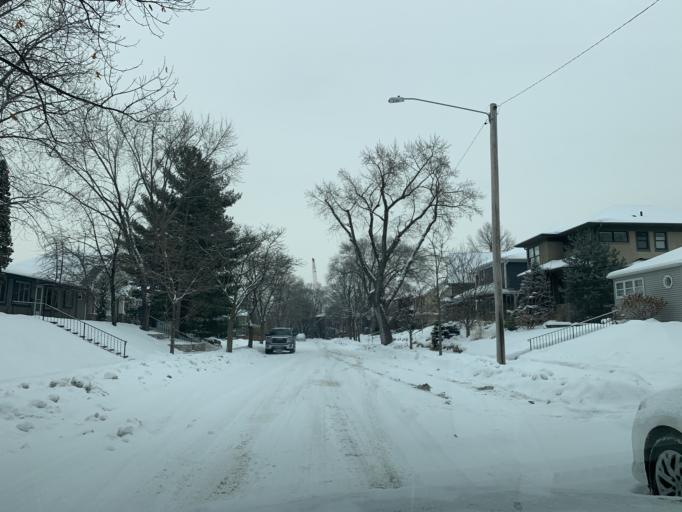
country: US
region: Minnesota
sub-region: Hennepin County
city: Saint Louis Park
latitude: 44.9514
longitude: -93.3232
